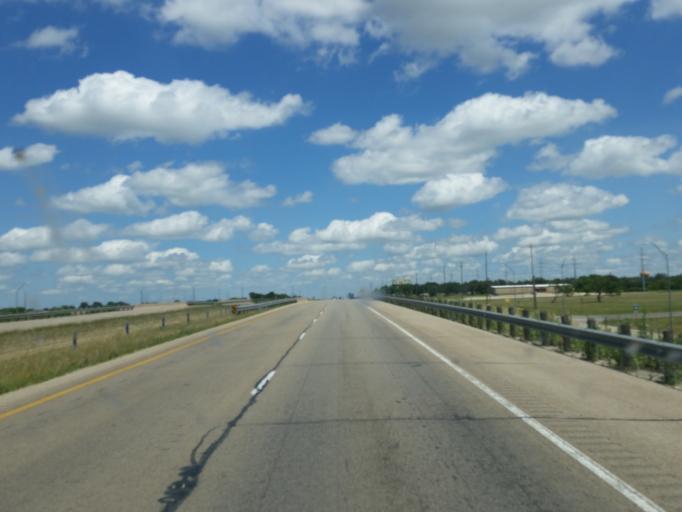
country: US
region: Texas
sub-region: Callahan County
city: Clyde
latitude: 32.4184
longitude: -99.5270
